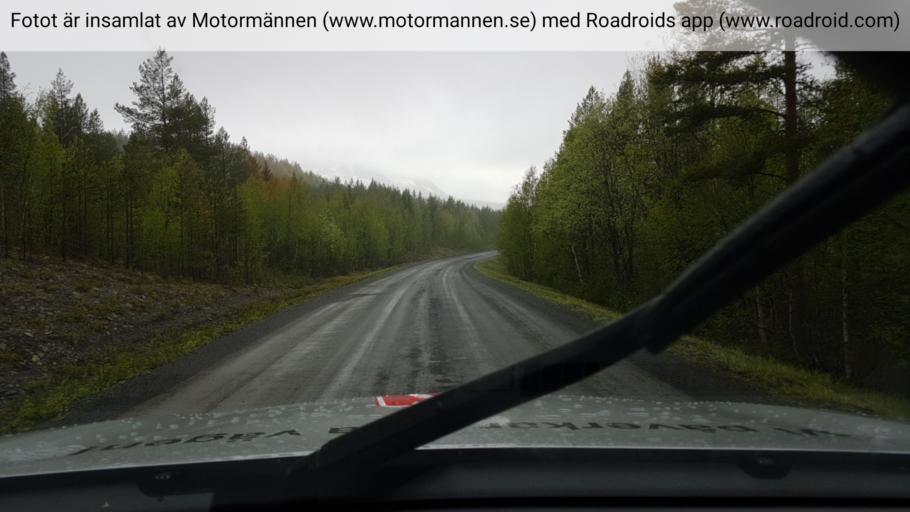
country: SE
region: Jaemtland
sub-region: Krokoms Kommun
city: Valla
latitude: 63.0809
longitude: 13.9350
